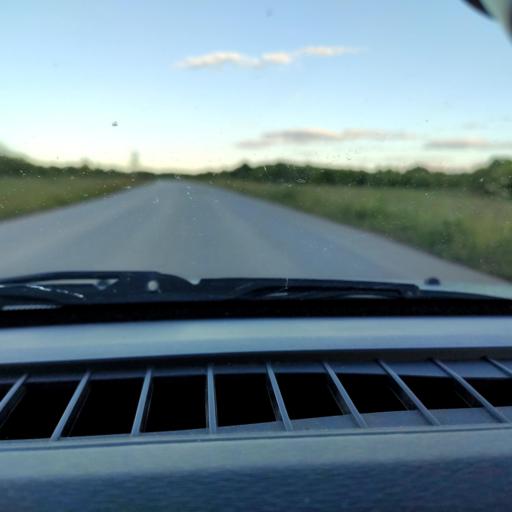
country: RU
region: Perm
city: Polazna
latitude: 58.2137
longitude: 56.4302
